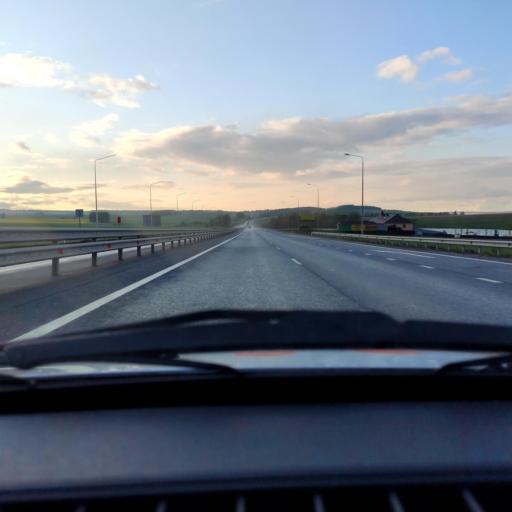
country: RU
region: Bashkortostan
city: Tolbazy
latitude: 53.9459
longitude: 55.9149
